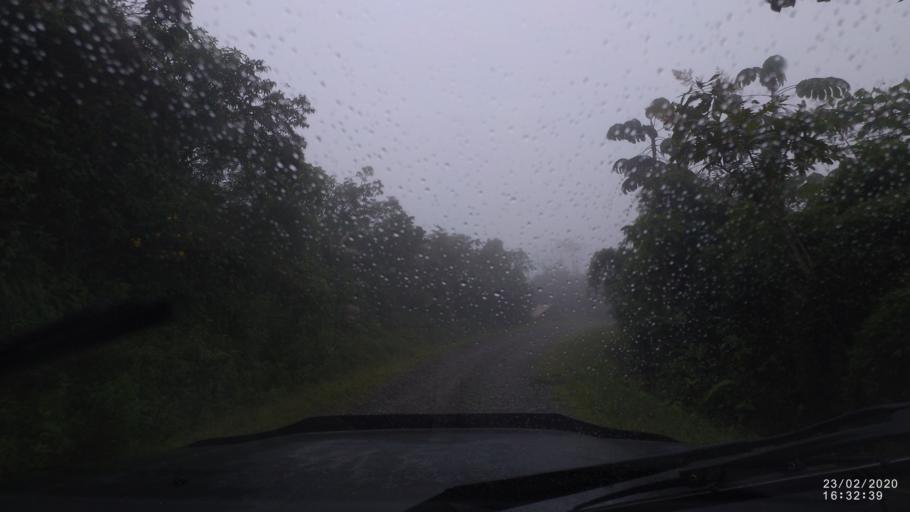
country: BO
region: Cochabamba
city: Colomi
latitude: -17.0932
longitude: -65.9923
